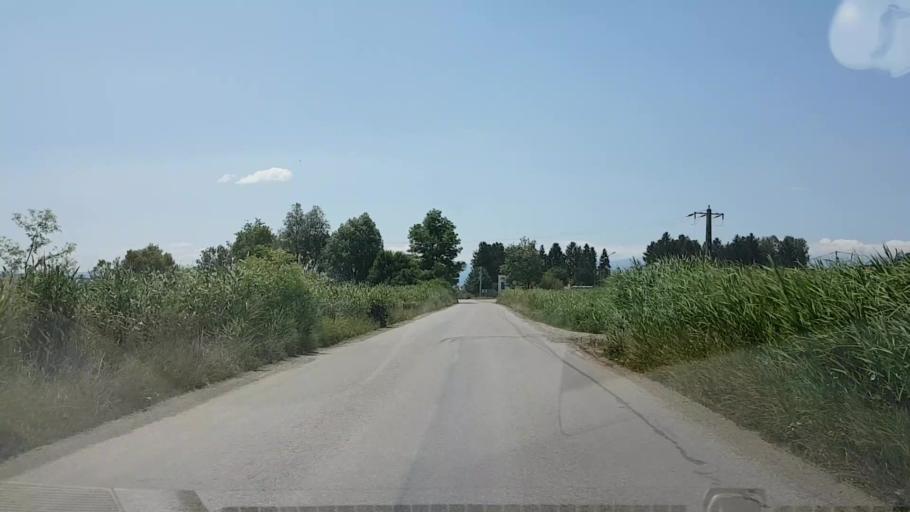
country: RO
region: Brasov
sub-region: Comuna Cincu
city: Cincu
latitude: 45.9267
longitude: 24.7962
